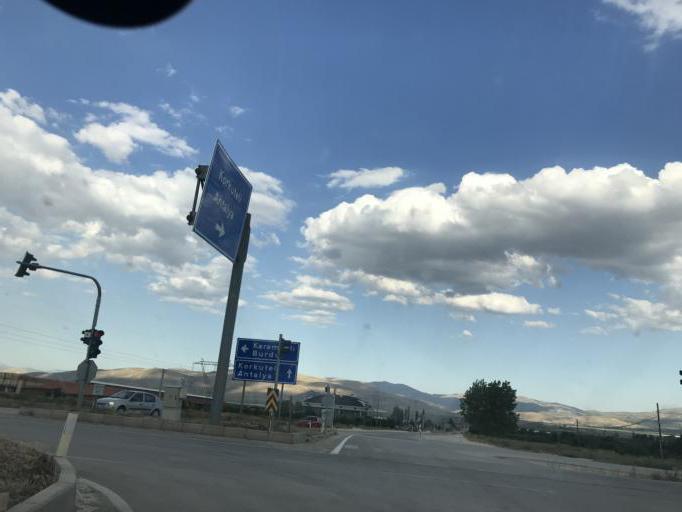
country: TR
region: Burdur
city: Tefenni
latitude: 37.3004
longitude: 29.7836
